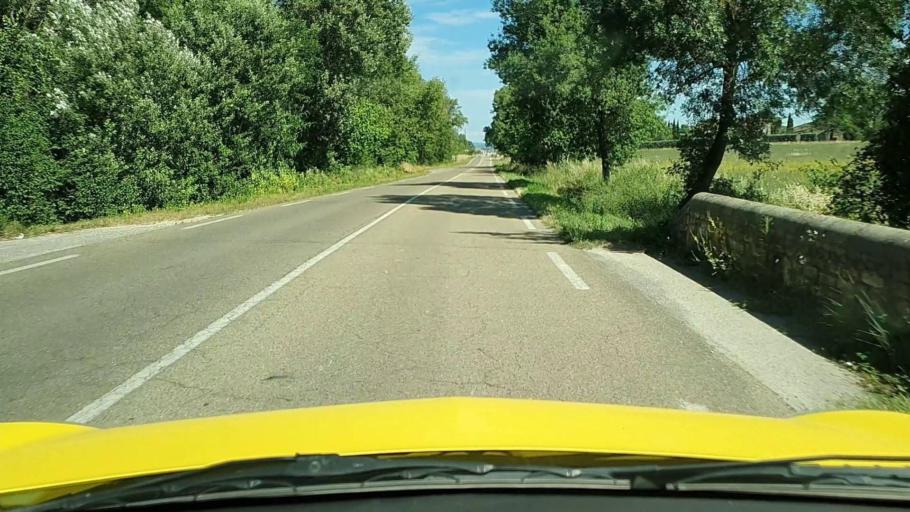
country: FR
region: Languedoc-Roussillon
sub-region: Departement du Gard
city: Saint-Hilaire-de-Brethmas
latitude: 44.0785
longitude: 4.1143
